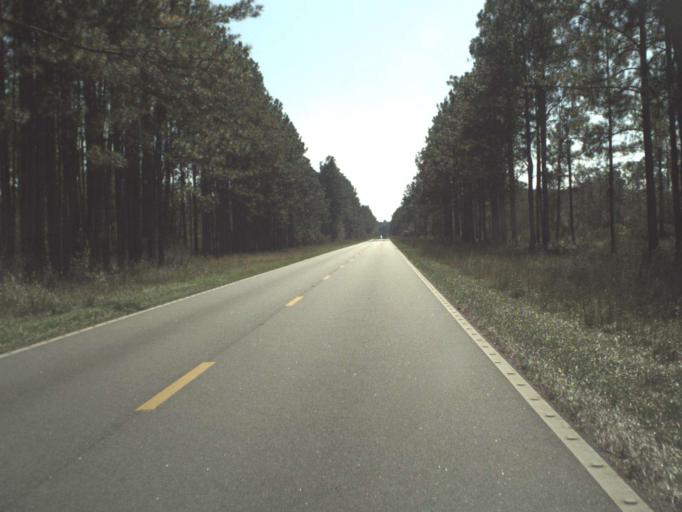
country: US
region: Florida
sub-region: Gulf County
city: Wewahitchka
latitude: 30.0430
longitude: -84.9836
